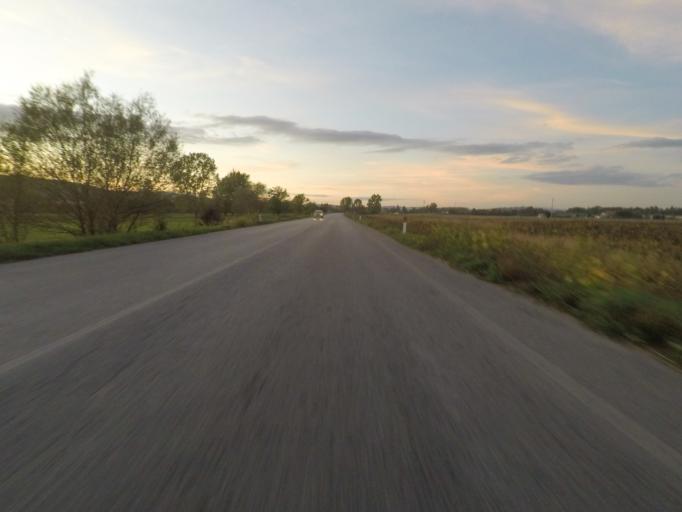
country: IT
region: Tuscany
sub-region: Provincia di Siena
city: Sinalunga
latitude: 43.2158
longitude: 11.7606
